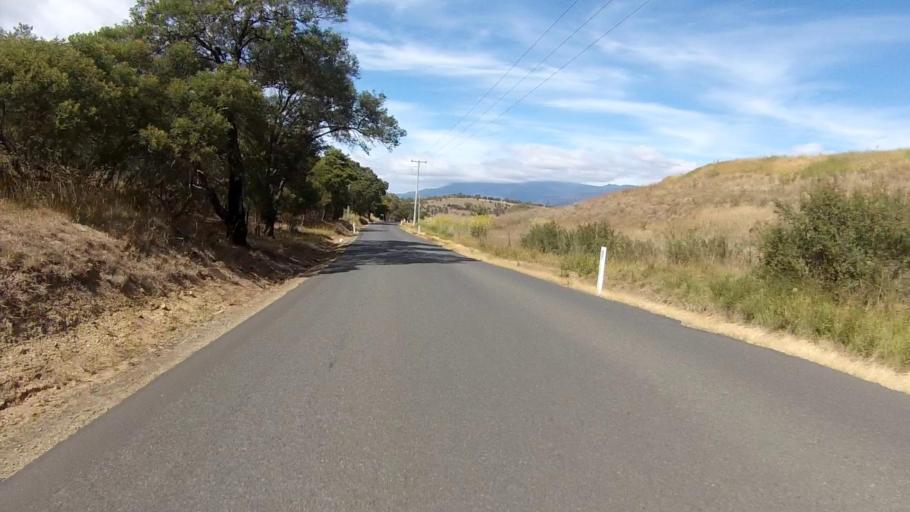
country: AU
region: Tasmania
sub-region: Brighton
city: Old Beach
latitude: -42.7445
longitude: 147.3017
